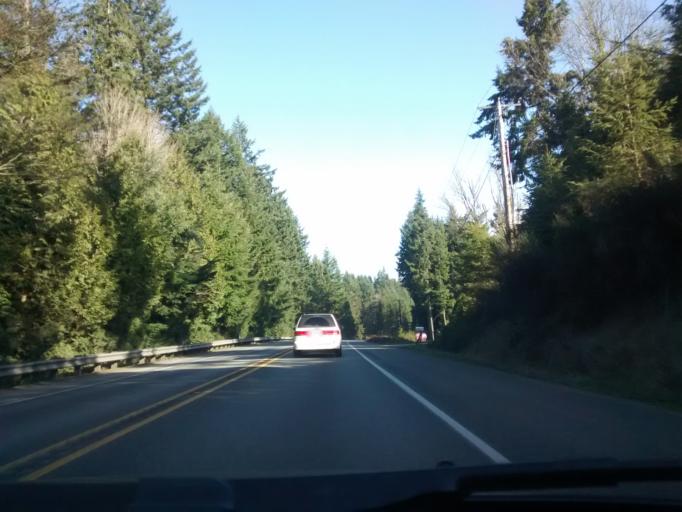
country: US
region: Washington
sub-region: Kitsap County
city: Lofall
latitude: 47.7935
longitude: -122.6516
